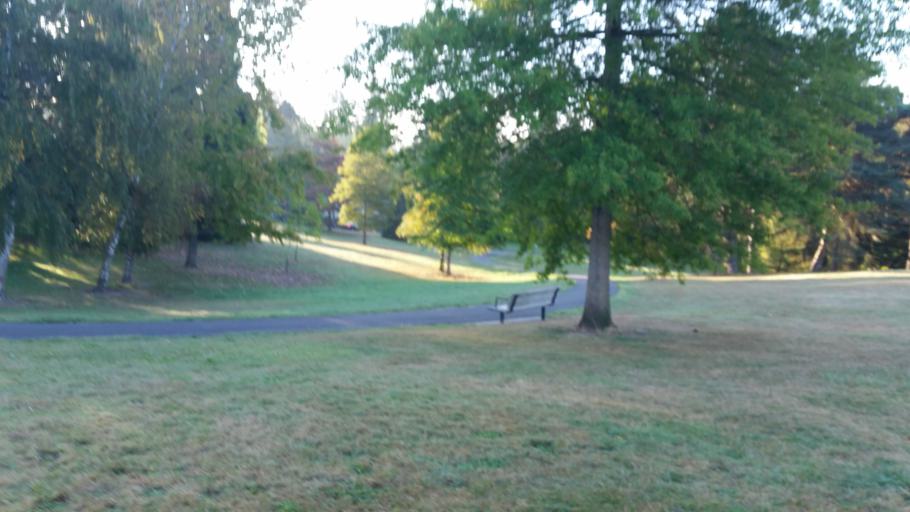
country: US
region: Oregon
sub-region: Washington County
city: Garden Home-Whitford
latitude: 45.4744
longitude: -122.7164
